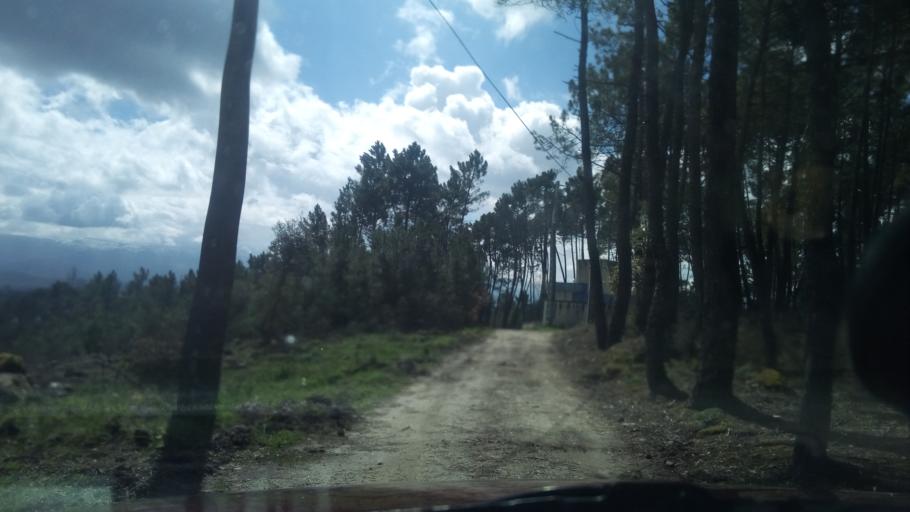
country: PT
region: Guarda
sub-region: Fornos de Algodres
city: Fornos de Algodres
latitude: 40.6253
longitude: -7.5238
